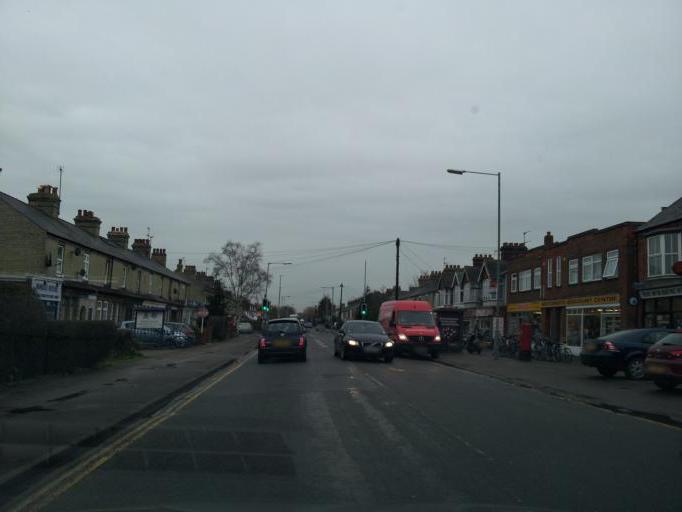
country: GB
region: England
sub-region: Cambridgeshire
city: Cambridge
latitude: 52.1877
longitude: 0.1468
